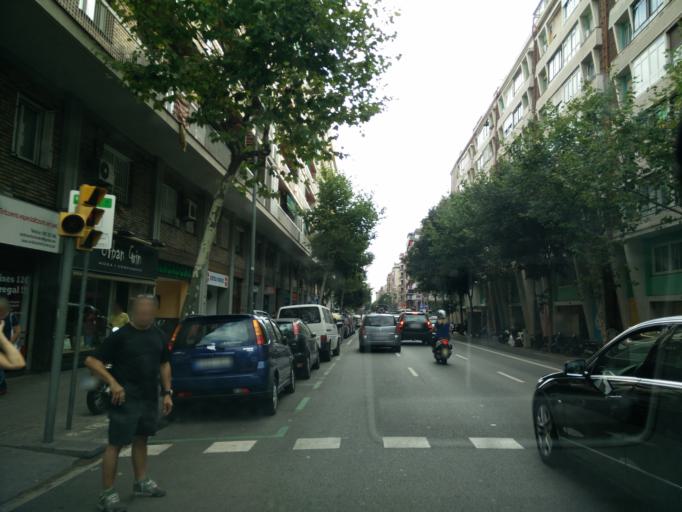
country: ES
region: Catalonia
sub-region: Provincia de Barcelona
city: Horta-Guinardo
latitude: 41.4061
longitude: 2.1815
